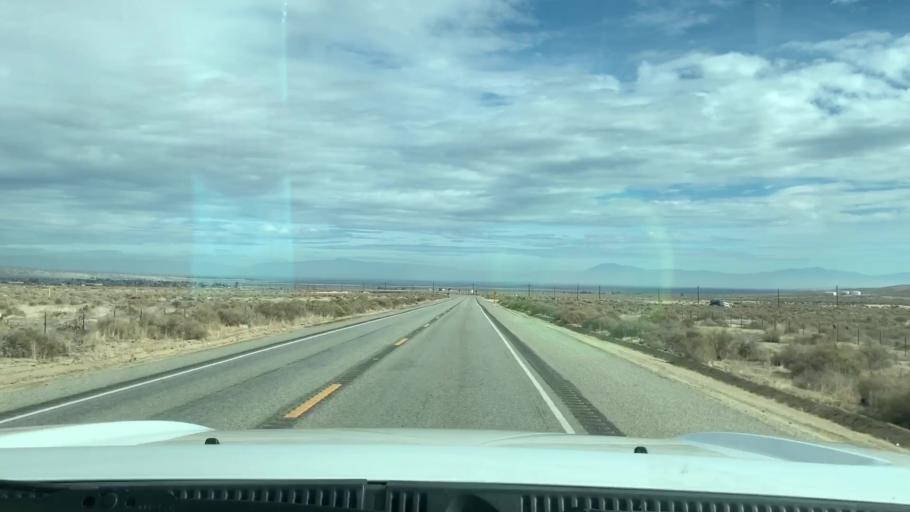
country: US
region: California
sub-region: Kern County
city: Ford City
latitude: 35.1873
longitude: -119.4424
